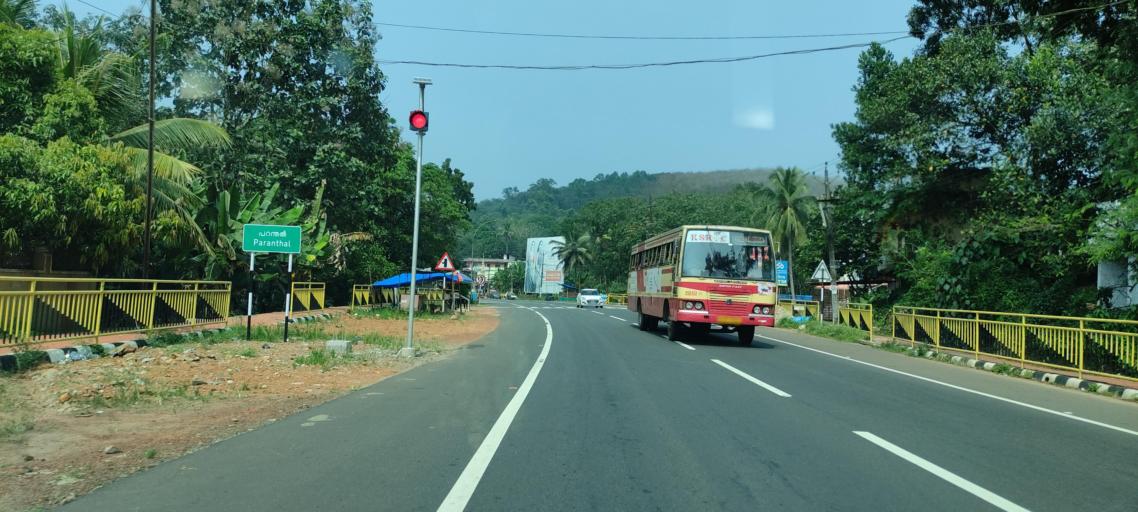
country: IN
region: Kerala
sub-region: Pattanamtitta
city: Adur
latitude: 9.1848
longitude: 76.7098
